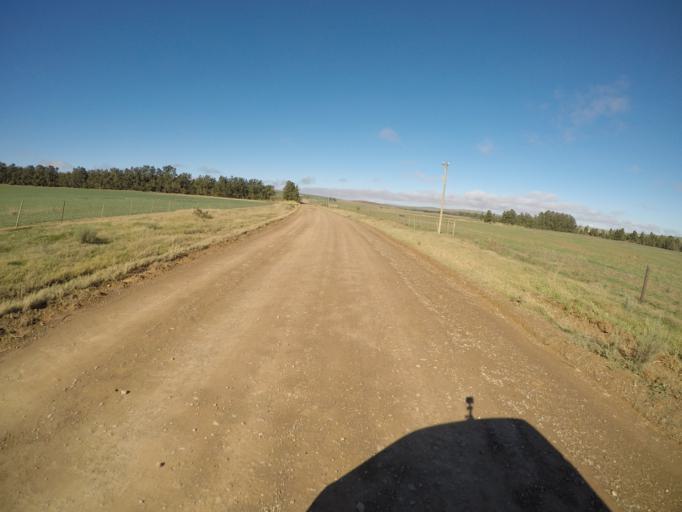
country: ZA
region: Western Cape
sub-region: Overberg District Municipality
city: Caledon
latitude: -34.0978
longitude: 19.6974
